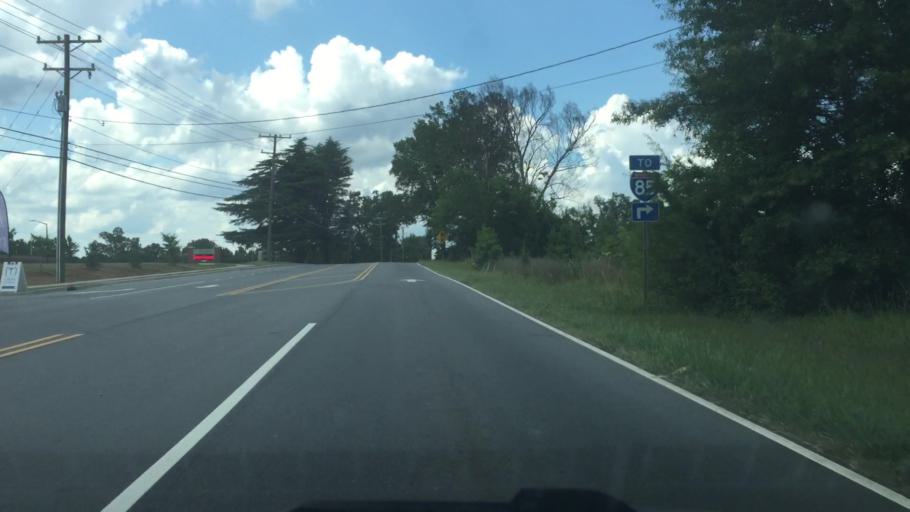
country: US
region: North Carolina
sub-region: Rowan County
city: Enochville
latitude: 35.4379
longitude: -80.7267
